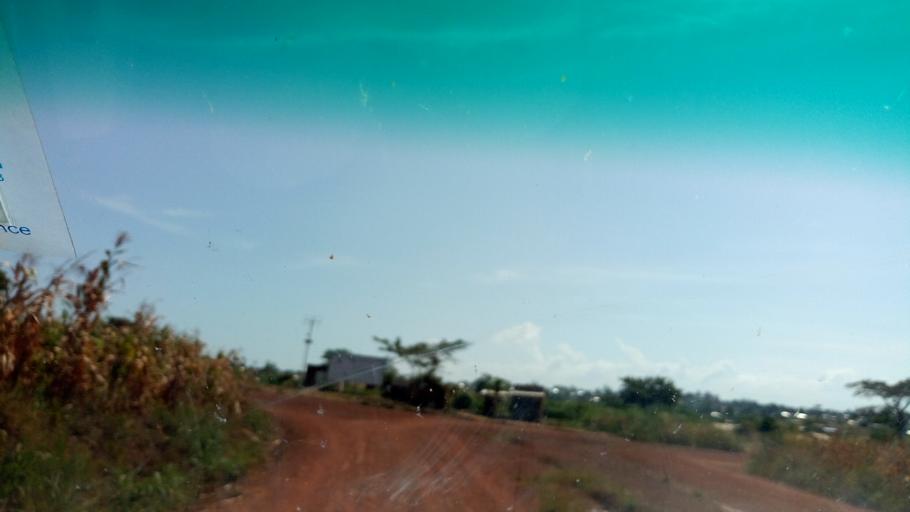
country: UG
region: Western Region
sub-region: Kiryandongo District
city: Kiryandongo
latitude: 1.9483
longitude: 32.1576
